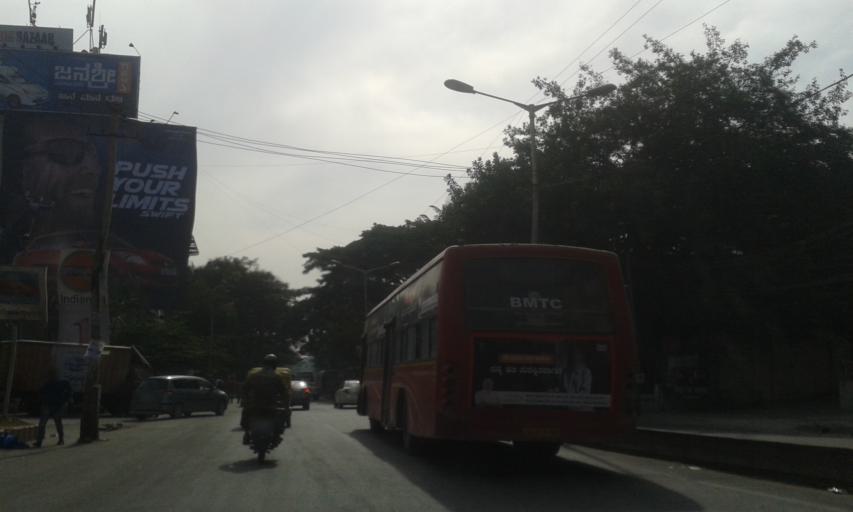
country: IN
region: Karnataka
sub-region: Bangalore Urban
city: Bangalore
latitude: 12.9337
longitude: 77.6112
